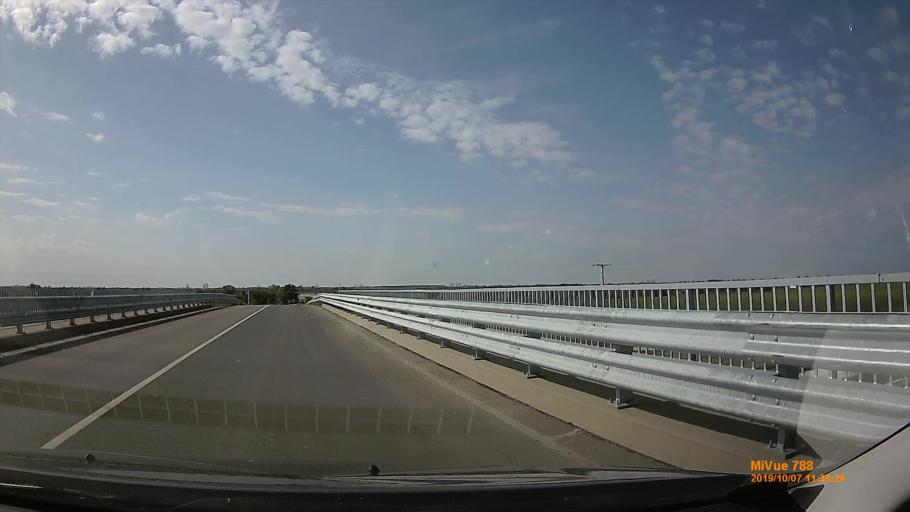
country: HU
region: Bekes
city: Kondoros
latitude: 46.7877
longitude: 20.7113
